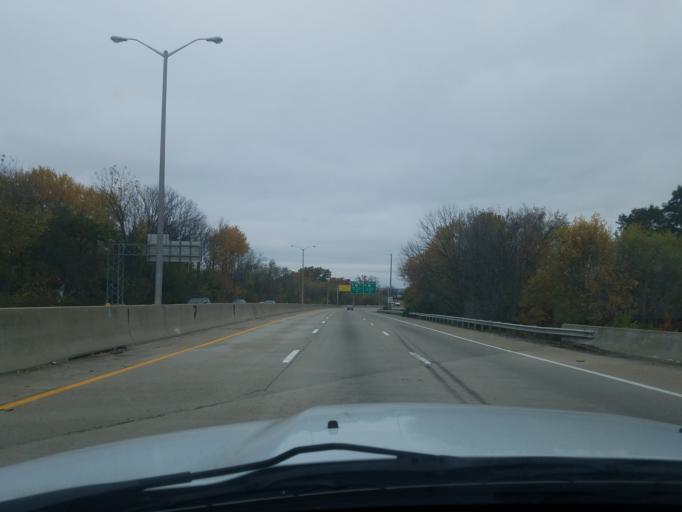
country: US
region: Indiana
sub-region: Floyd County
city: New Albany
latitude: 38.2654
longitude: -85.8067
